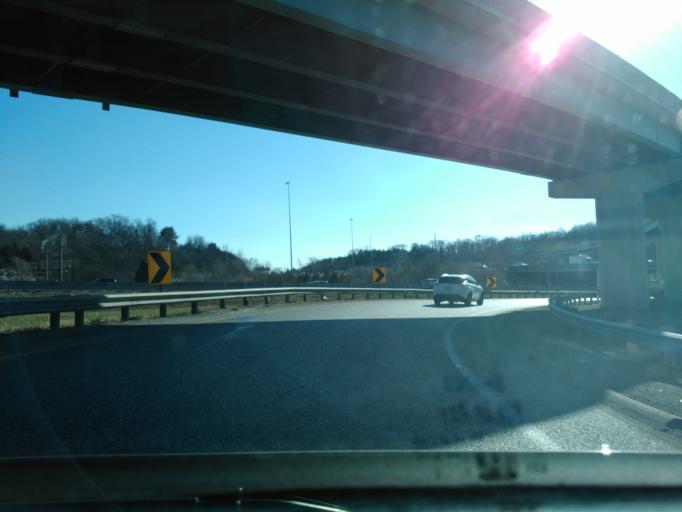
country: US
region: Missouri
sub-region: Saint Louis County
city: Sunset Hills
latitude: 38.5500
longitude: -90.4264
